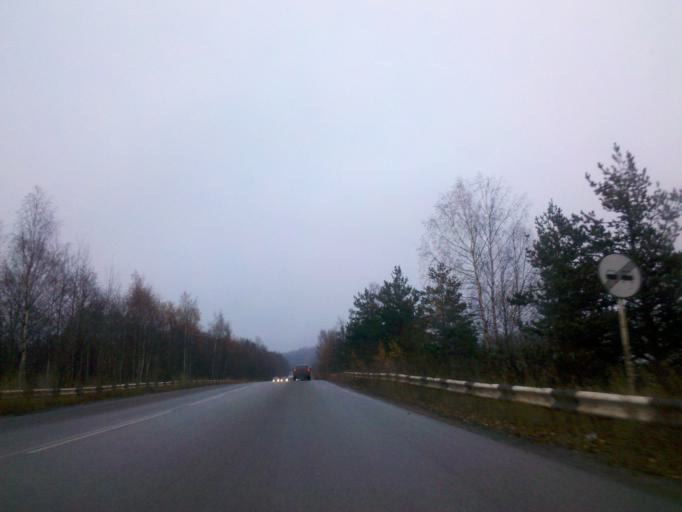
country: RU
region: Republic of Karelia
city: Petrozavodsk
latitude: 61.8231
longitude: 34.2279
